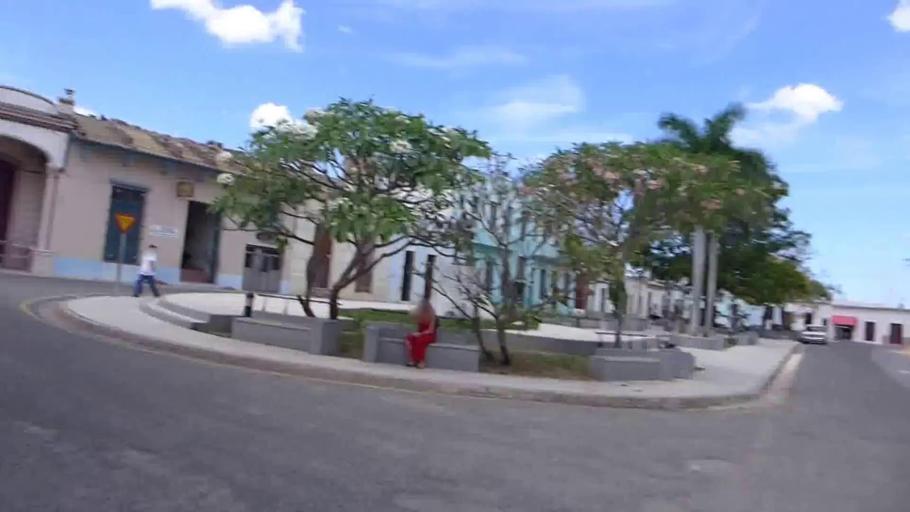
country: CU
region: Camaguey
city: Camaguey
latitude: 21.3831
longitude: -77.9191
